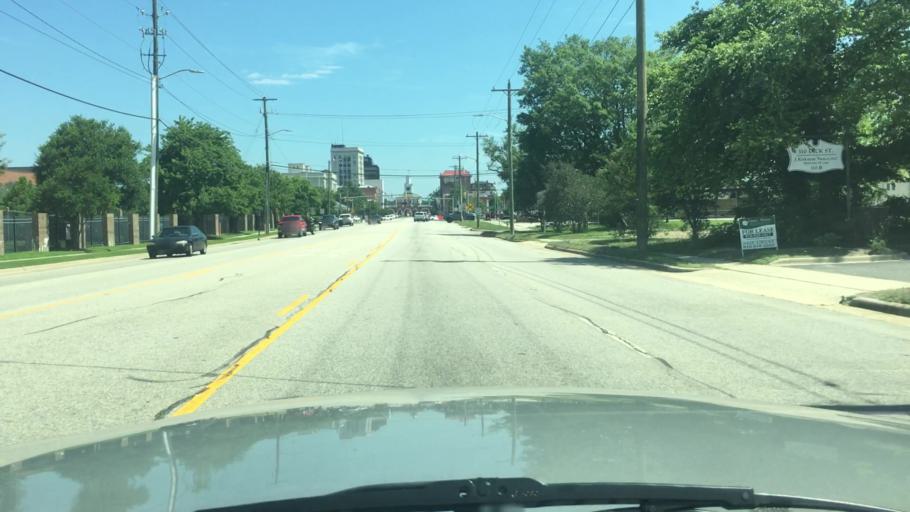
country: US
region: North Carolina
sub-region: Cumberland County
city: Fayetteville
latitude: 35.0485
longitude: -78.8797
